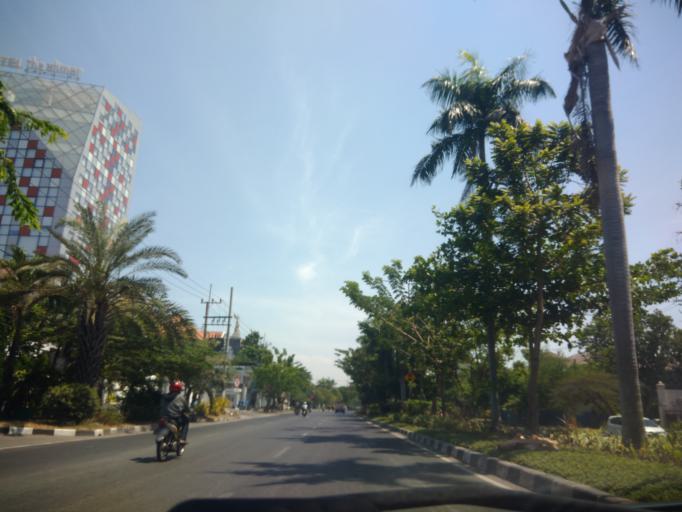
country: ID
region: East Java
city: Mulyorejo
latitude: -7.2717
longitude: 112.7818
